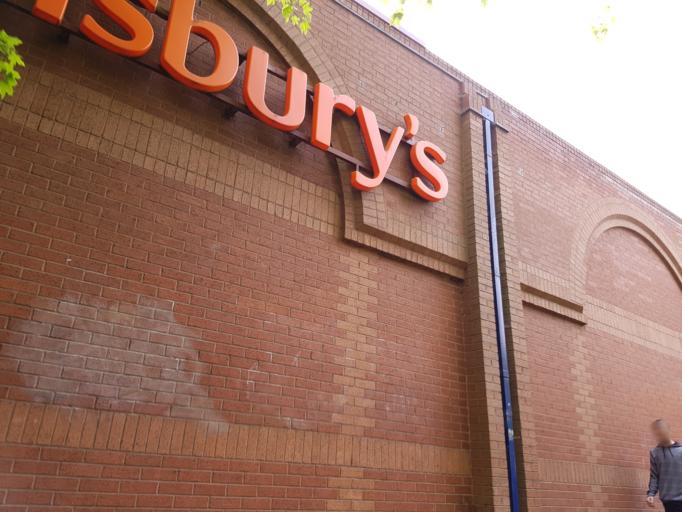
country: GB
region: England
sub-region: Nottingham
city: Nottingham
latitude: 52.9470
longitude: -1.1623
